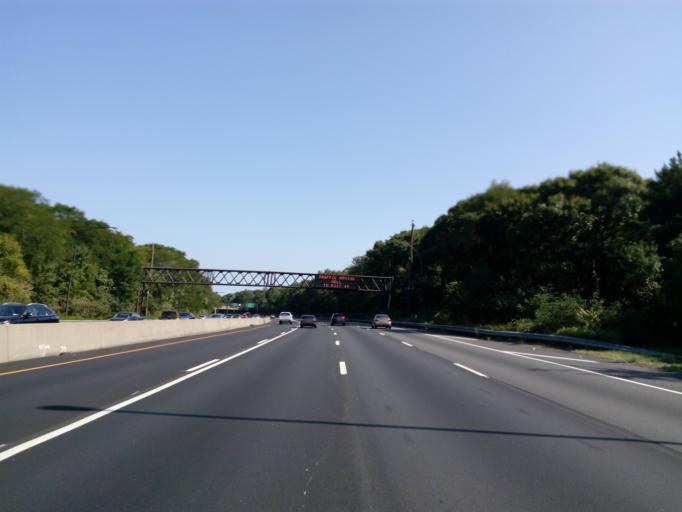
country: US
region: New York
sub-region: Nassau County
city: Old Westbury
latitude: 40.7809
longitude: -73.5822
